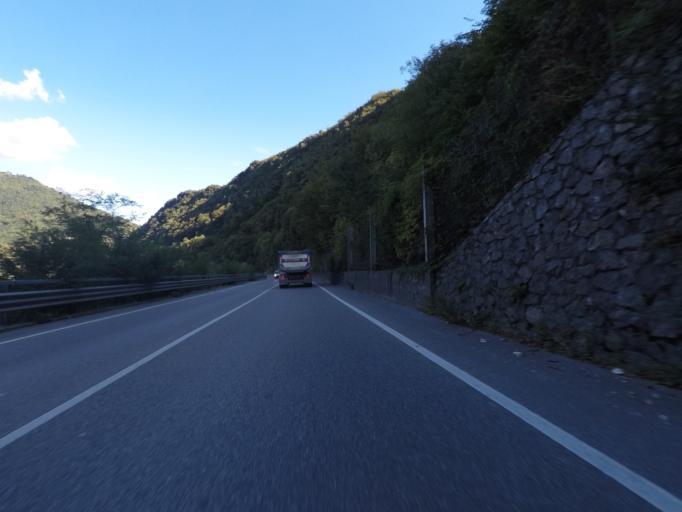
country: IT
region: Tuscany
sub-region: Provincia di Lucca
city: Valdottavo
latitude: 43.9362
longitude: 10.4986
